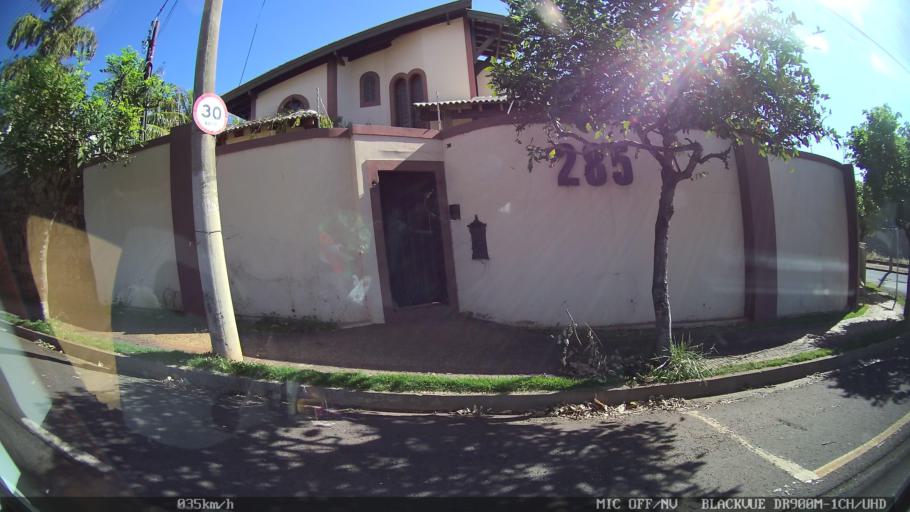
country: BR
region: Sao Paulo
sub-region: Olimpia
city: Olimpia
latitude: -20.7326
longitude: -48.9190
